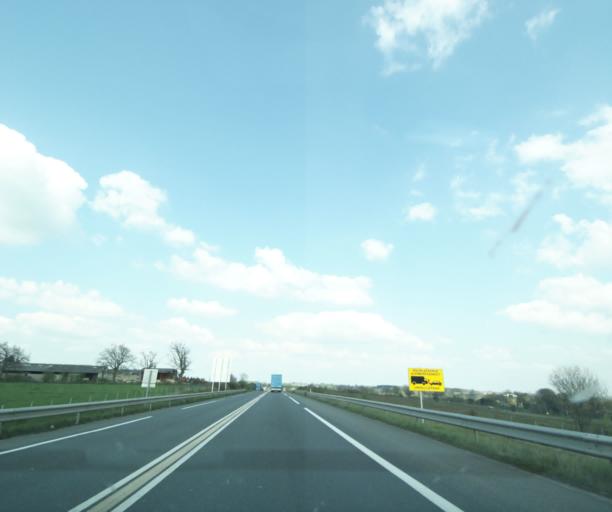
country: FR
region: Auvergne
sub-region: Departement de l'Allier
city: Montmarault
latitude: 46.3329
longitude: 2.9759
